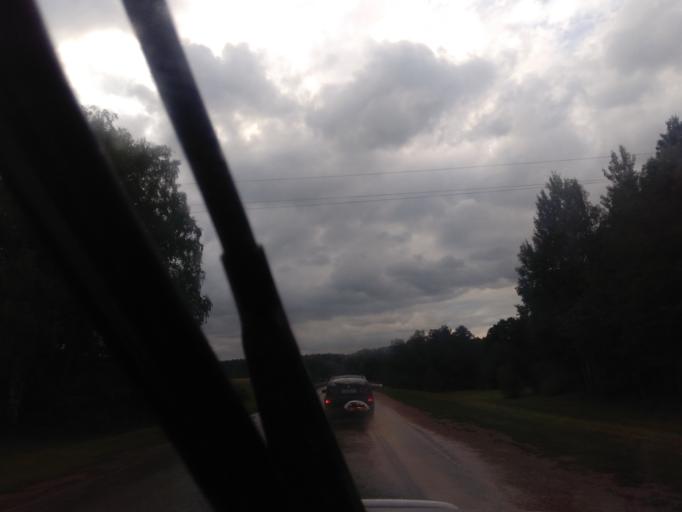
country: BY
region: Minsk
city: Enyerhyetykaw
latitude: 53.5393
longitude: 27.0627
